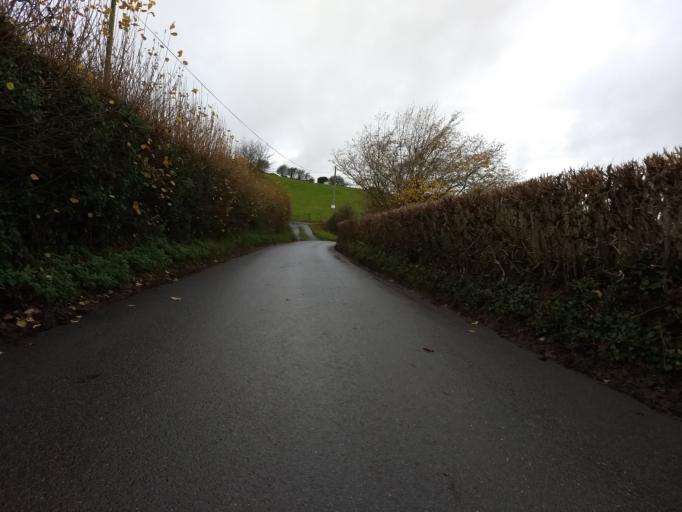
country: GB
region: England
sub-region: Isle of Wight
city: Newport
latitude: 50.6853
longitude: -1.2600
